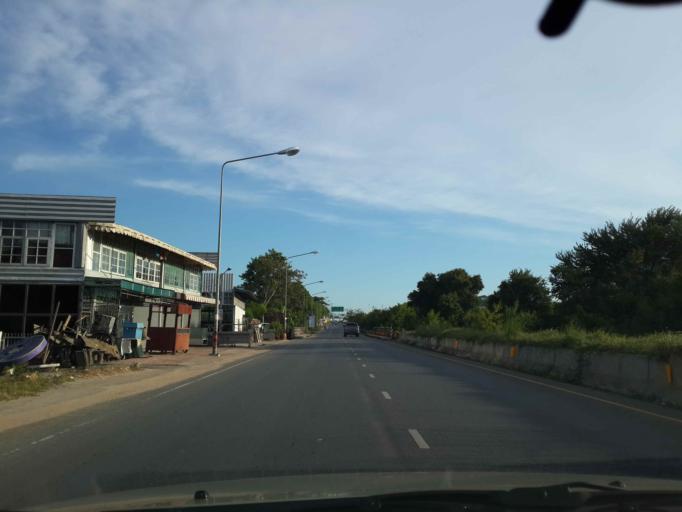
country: TH
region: Chon Buri
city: Phatthaya
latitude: 12.9529
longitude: 100.9160
